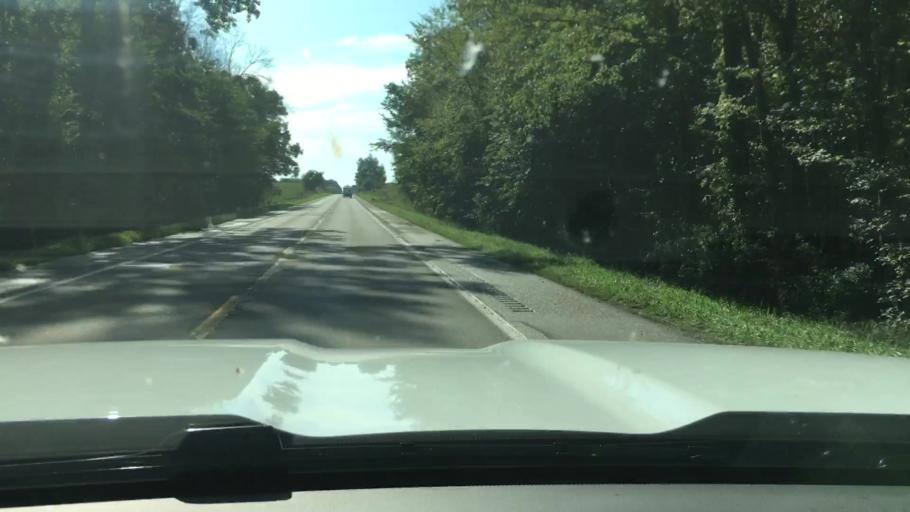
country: US
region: Michigan
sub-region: Montcalm County
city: Edmore
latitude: 43.4236
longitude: -85.1427
